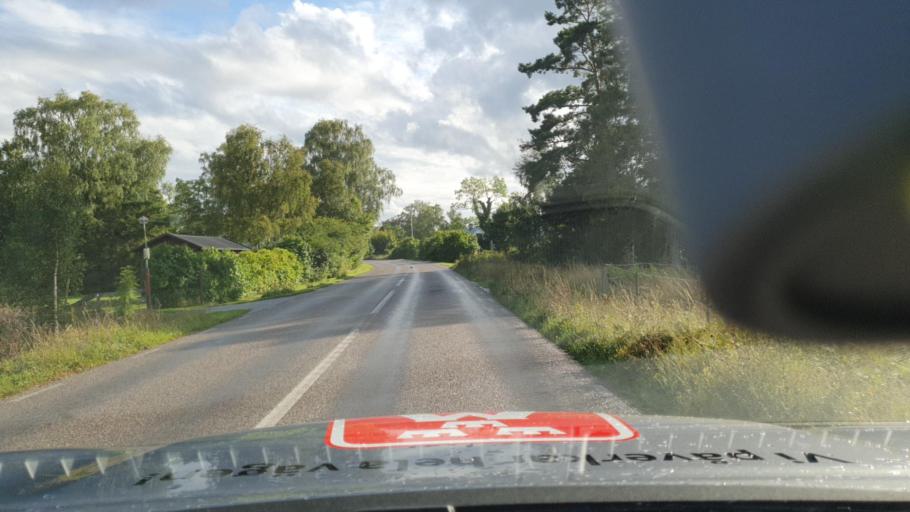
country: SE
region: Gotland
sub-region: Gotland
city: Slite
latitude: 57.6552
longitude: 18.7693
